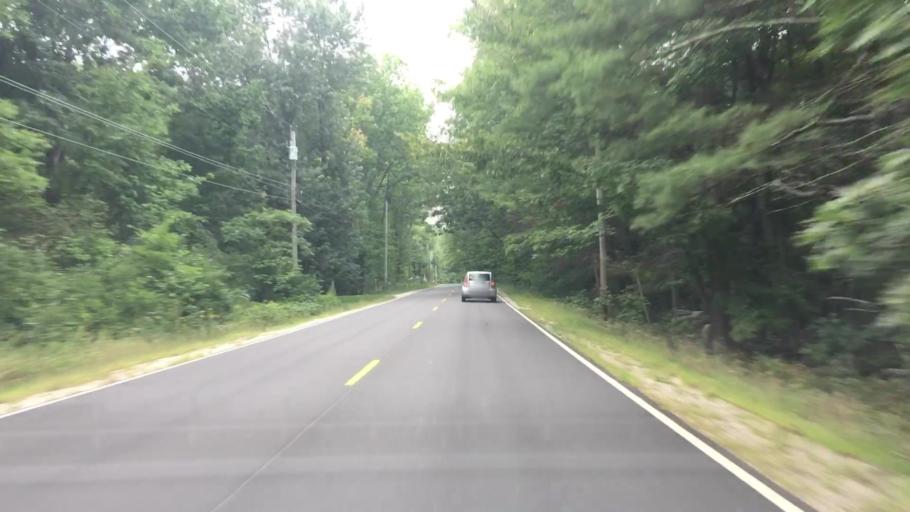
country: US
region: Maine
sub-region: Cumberland County
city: New Gloucester
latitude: 43.8840
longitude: -70.2497
